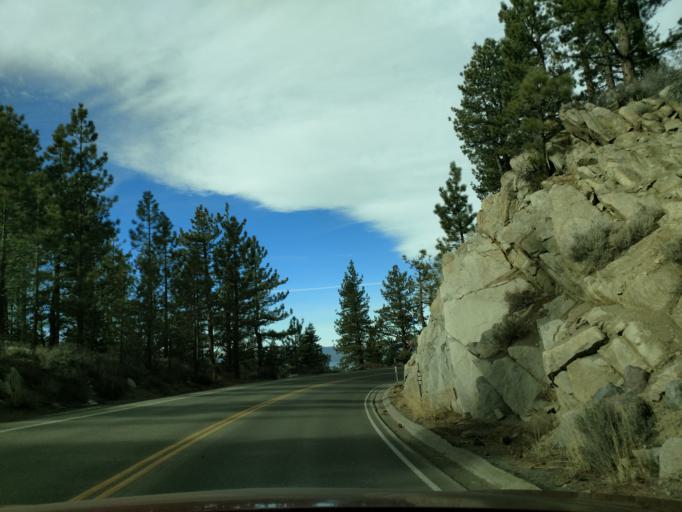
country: US
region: Nevada
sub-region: Douglas County
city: Kingsbury
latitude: 39.1147
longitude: -119.9258
